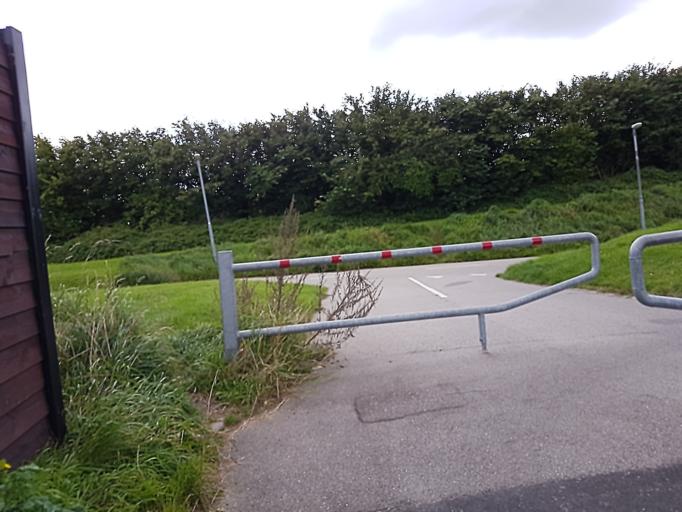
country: DK
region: Zealand
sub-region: Roskilde Kommune
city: Jyllinge
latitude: 55.7526
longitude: 12.1126
